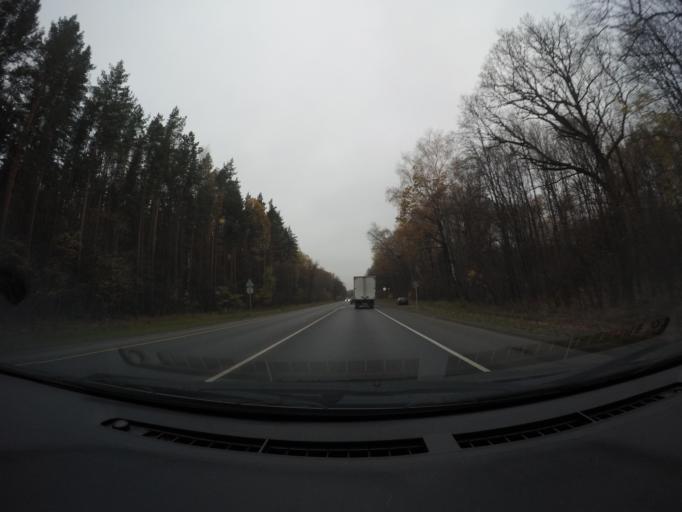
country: RU
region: Moskovskaya
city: Bronnitsy
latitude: 55.3954
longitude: 38.2175
